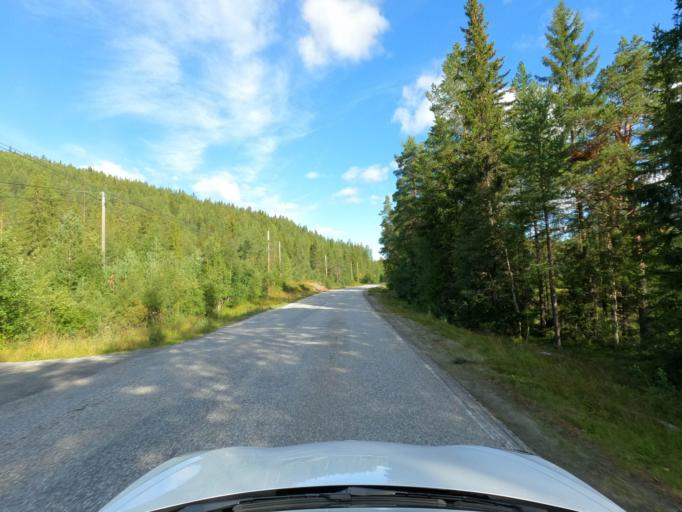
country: NO
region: Telemark
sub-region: Tinn
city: Rjukan
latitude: 59.9631
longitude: 8.8769
